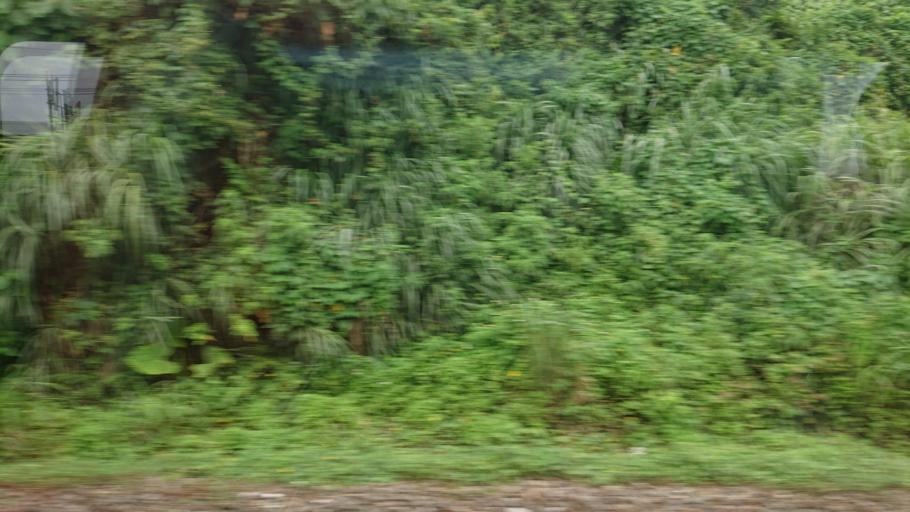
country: TW
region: Taiwan
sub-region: Keelung
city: Keelung
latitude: 24.9623
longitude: 121.9202
